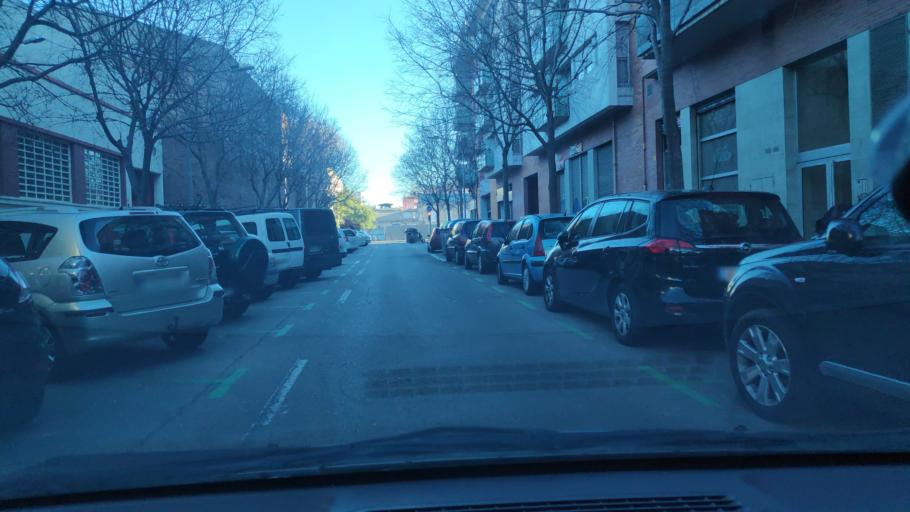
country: ES
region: Catalonia
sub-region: Provincia de Barcelona
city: Sant Marti
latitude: 41.4070
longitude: 2.1964
